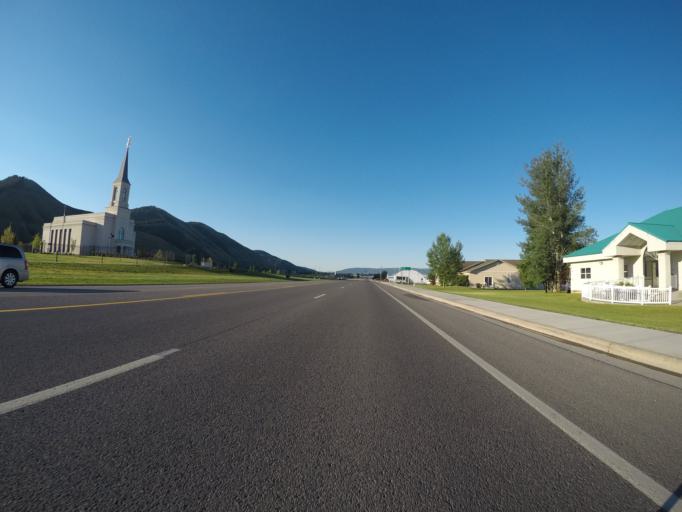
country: US
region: Wyoming
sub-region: Lincoln County
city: Afton
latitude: 42.7127
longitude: -110.9336
